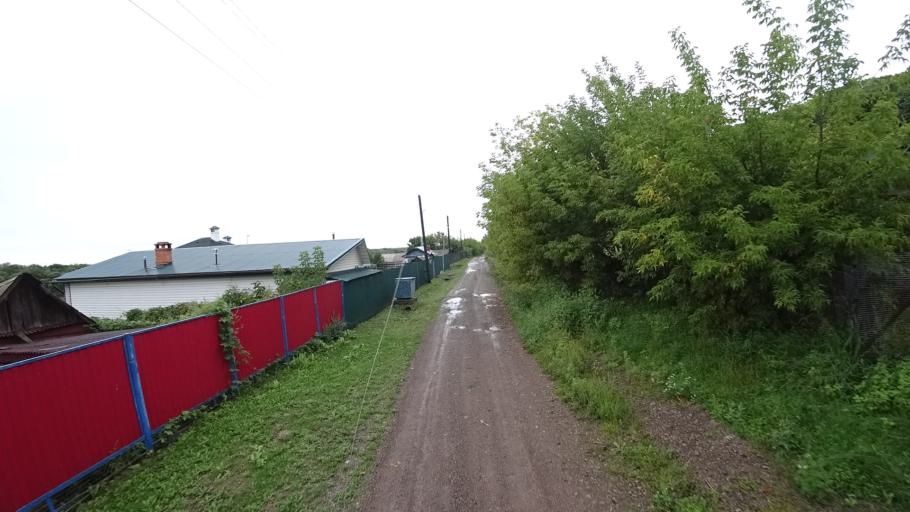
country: RU
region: Primorskiy
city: Monastyrishche
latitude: 44.2643
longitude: 132.4044
